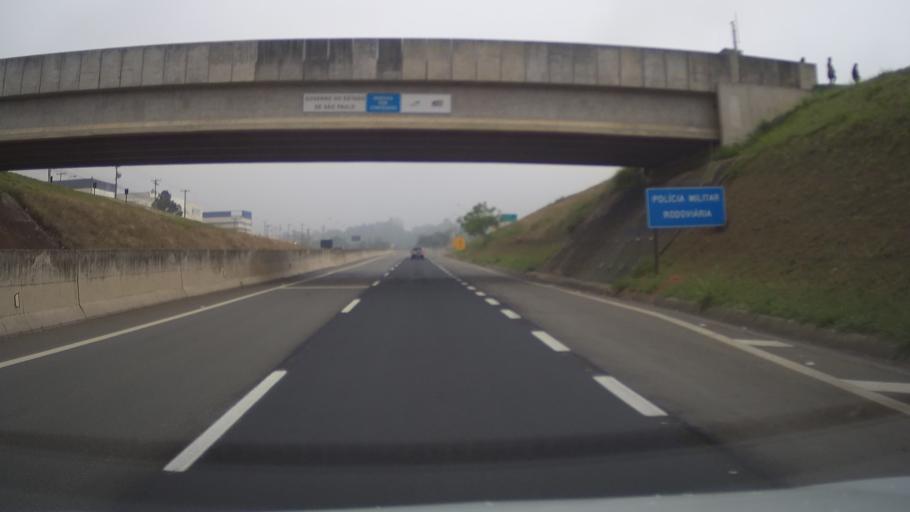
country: BR
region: Sao Paulo
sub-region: Itatiba
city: Itatiba
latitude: -23.0652
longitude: -46.8400
